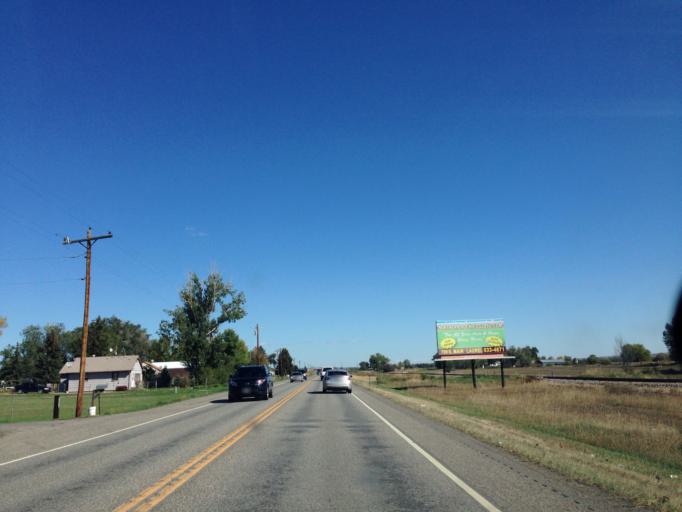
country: US
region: Montana
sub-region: Yellowstone County
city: Laurel
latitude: 45.6281
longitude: -108.7754
